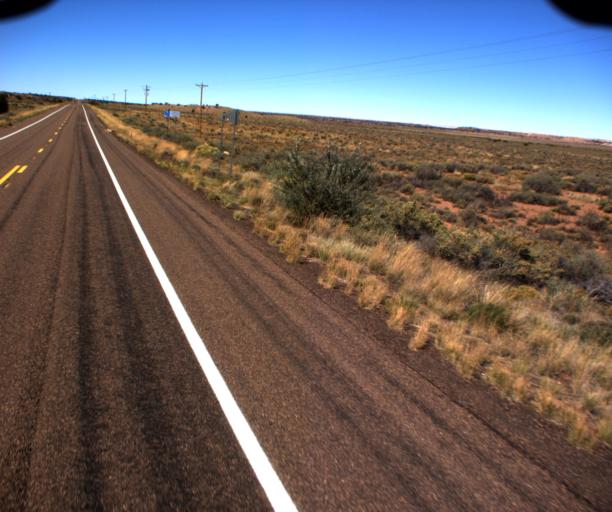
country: US
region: Arizona
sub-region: Apache County
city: Saint Johns
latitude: 34.6208
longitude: -109.6634
